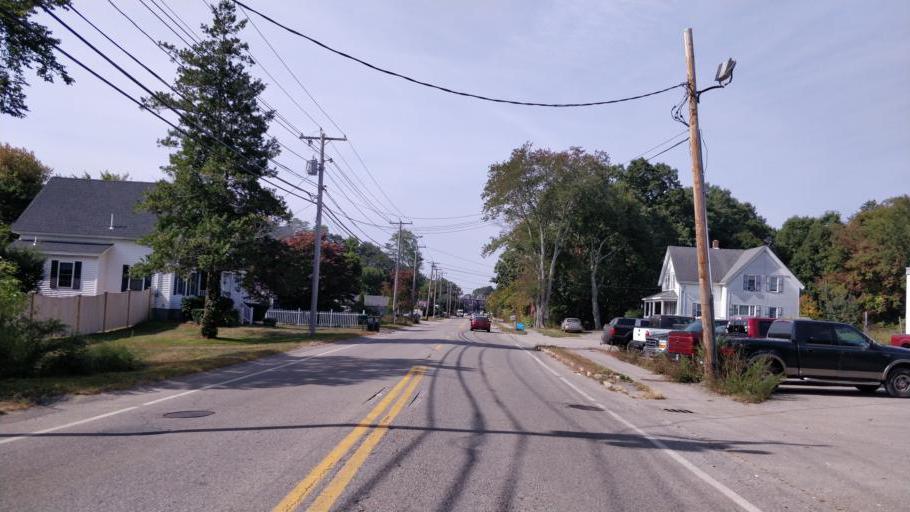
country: US
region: Massachusetts
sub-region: Bristol County
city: Norton
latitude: 41.9529
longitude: -71.2214
